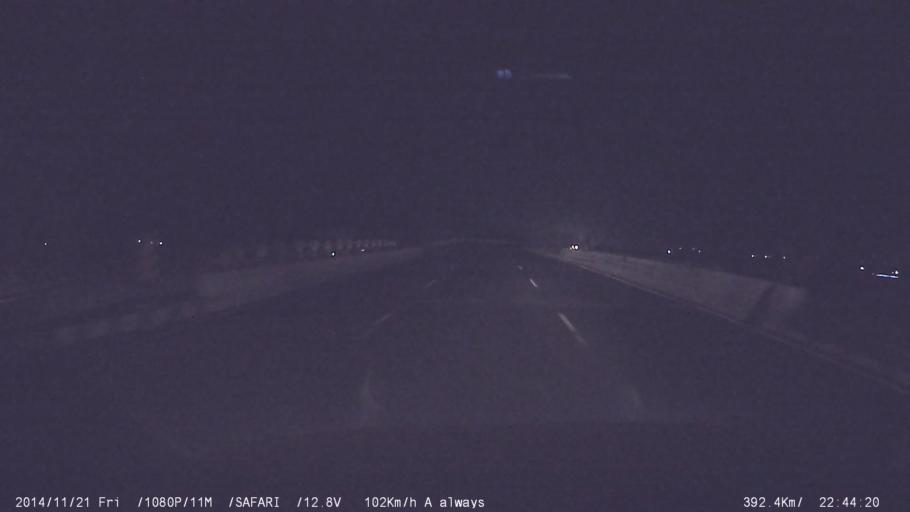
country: IN
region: Tamil Nadu
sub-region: Villupuram
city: Tindivanam
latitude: 12.2174
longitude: 79.6598
